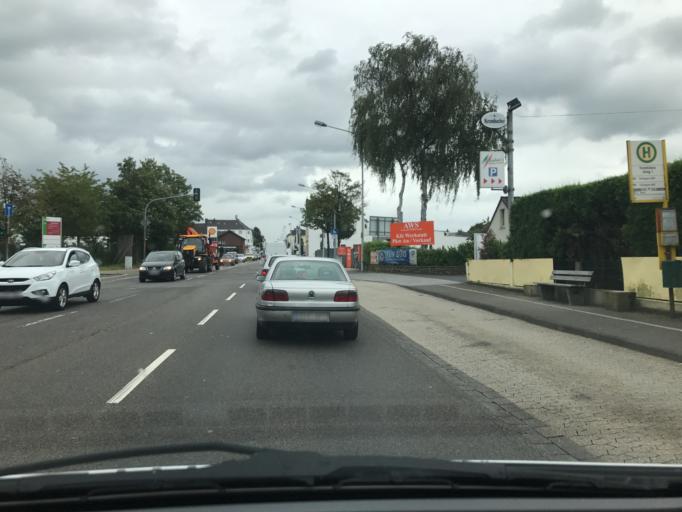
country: DE
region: North Rhine-Westphalia
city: Haan
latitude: 51.1677
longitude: 6.9816
